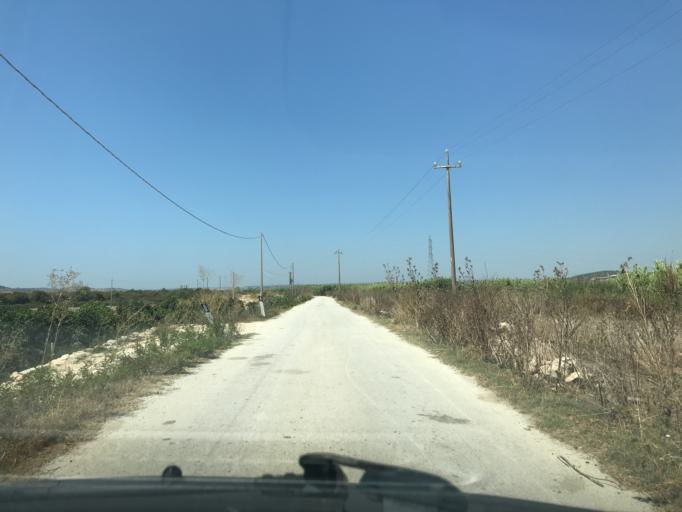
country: IT
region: Sicily
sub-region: Provincia di Siracusa
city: Noto
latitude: 36.8368
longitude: 15.0603
